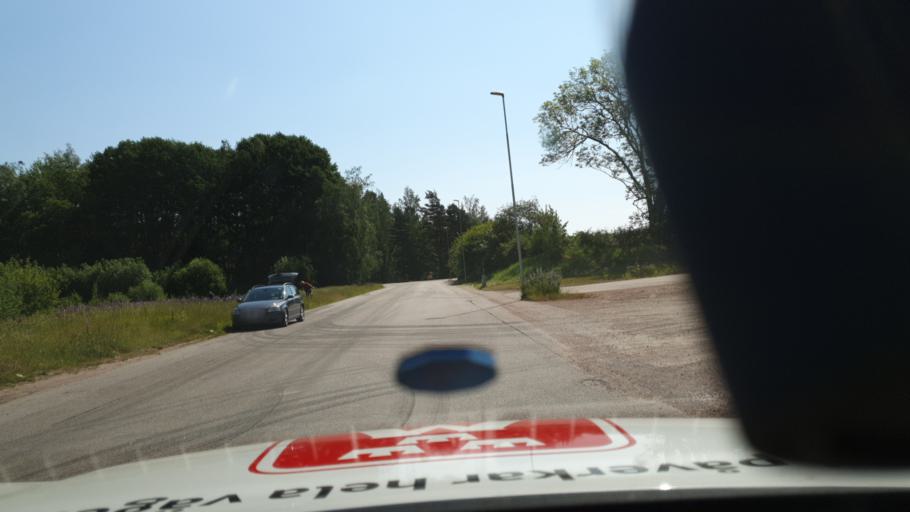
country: SE
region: Vaestra Goetaland
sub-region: Tibro Kommun
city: Tibro
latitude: 58.4082
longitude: 14.1493
